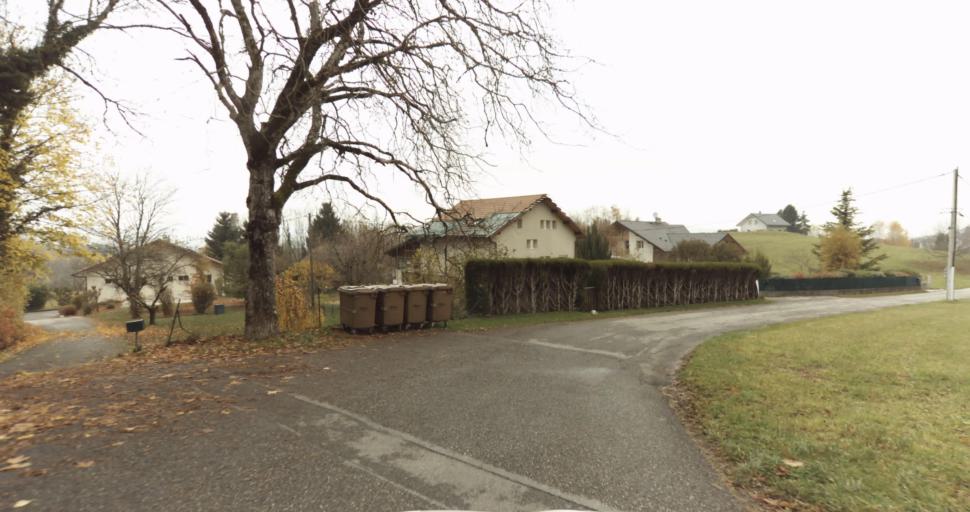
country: FR
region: Rhone-Alpes
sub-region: Departement de la Haute-Savoie
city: Viuz-la-Chiesaz
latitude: 45.8060
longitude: 6.0631
